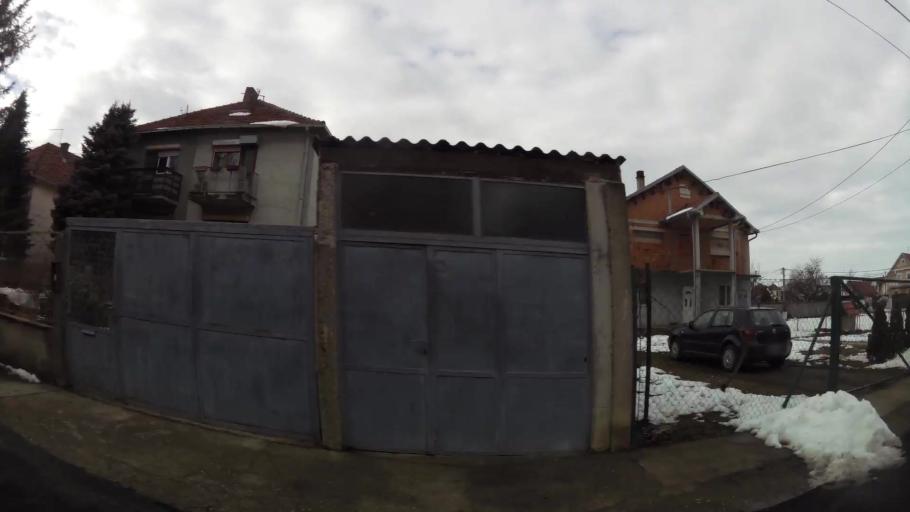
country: RS
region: Central Serbia
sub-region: Belgrade
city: Surcin
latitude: 44.8006
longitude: 20.2965
